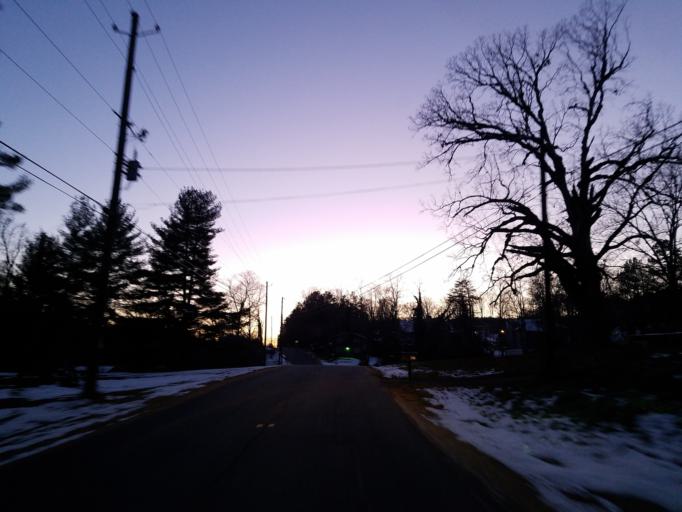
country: US
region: Georgia
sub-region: Cherokee County
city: Ball Ground
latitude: 34.3436
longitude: -84.3679
